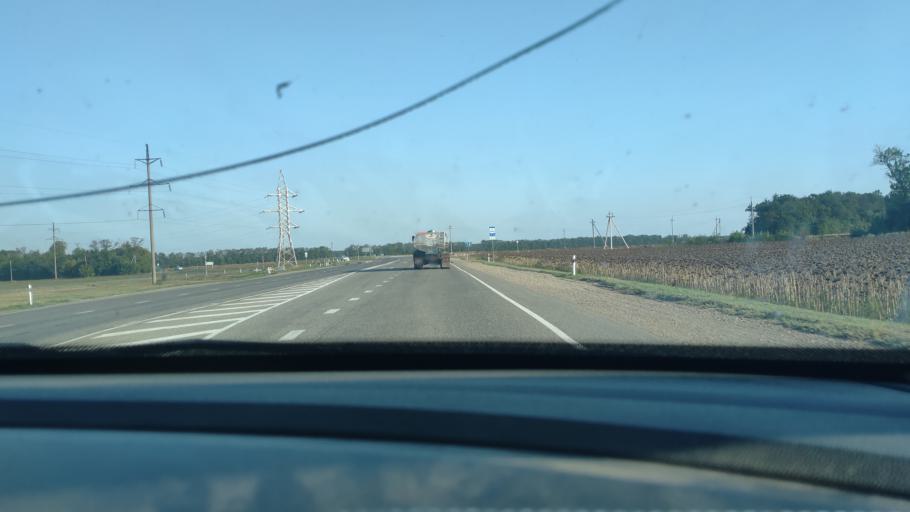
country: RU
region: Krasnodarskiy
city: Starominskaya
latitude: 46.5039
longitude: 39.0376
